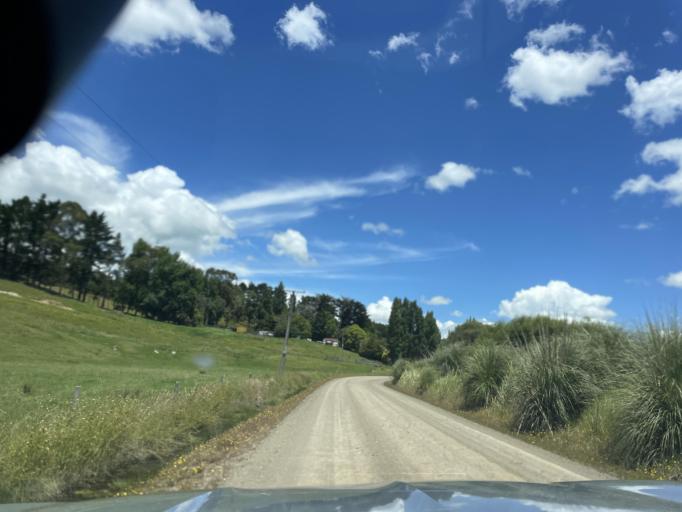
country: NZ
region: Northland
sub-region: Kaipara District
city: Dargaville
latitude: -35.9050
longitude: 173.9225
